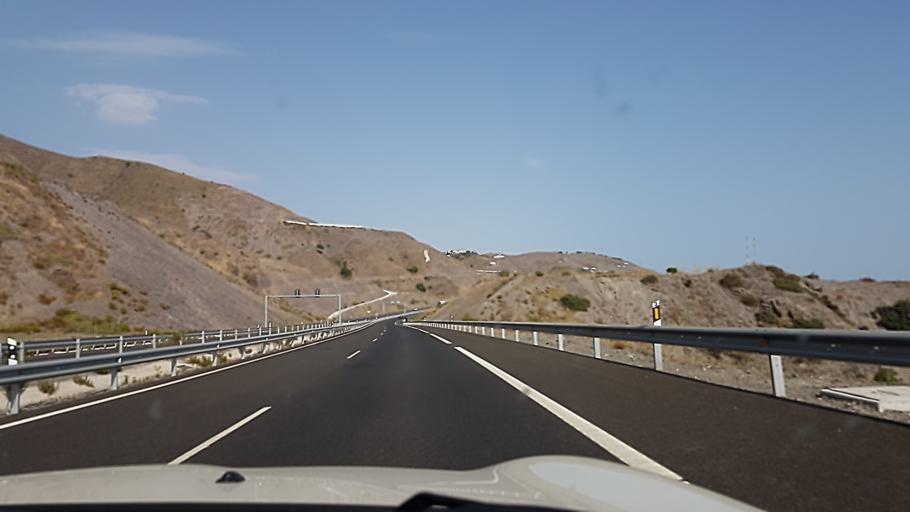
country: ES
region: Andalusia
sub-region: Provincia de Granada
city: Sorvilan
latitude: 36.7569
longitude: -3.2433
